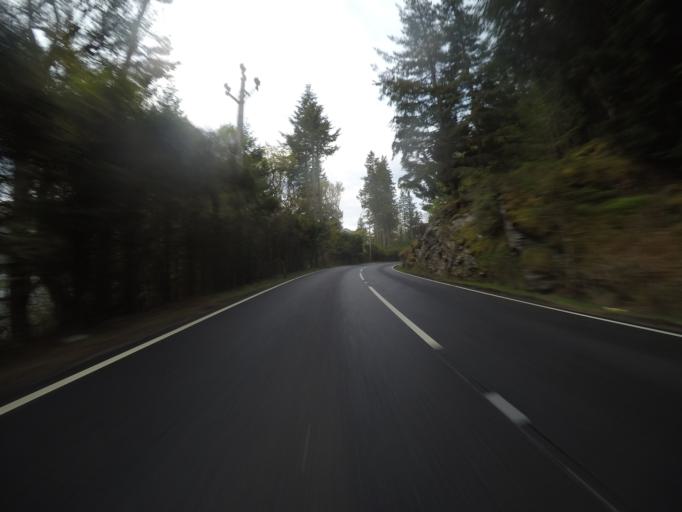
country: GB
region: Scotland
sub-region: Highland
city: Beauly
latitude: 57.1879
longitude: -4.6192
